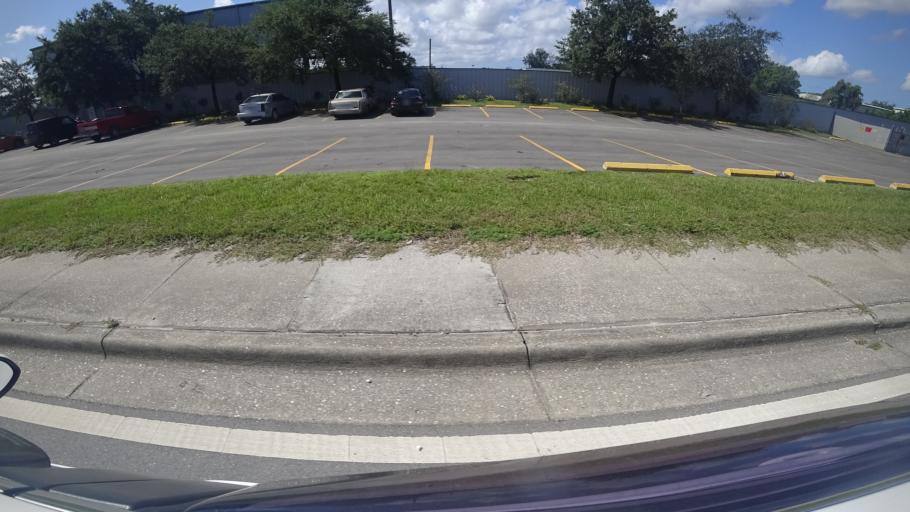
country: US
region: Florida
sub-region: Manatee County
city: Whitfield
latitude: 27.4292
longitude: -82.5419
